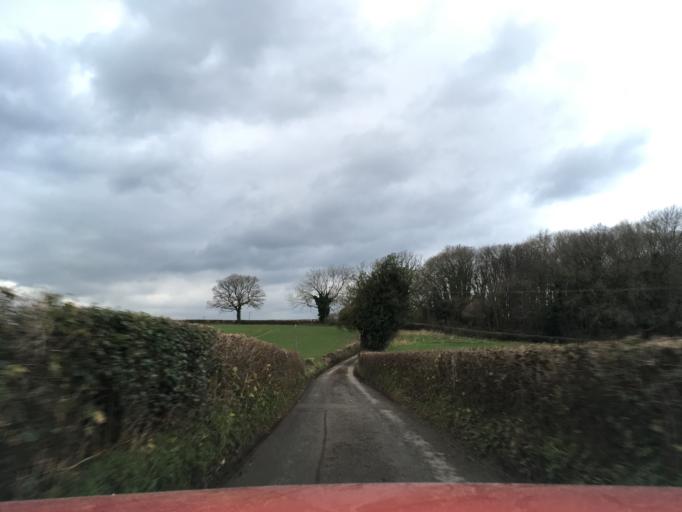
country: GB
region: Wales
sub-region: Newport
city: Llanvaches
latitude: 51.6096
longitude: -2.8047
